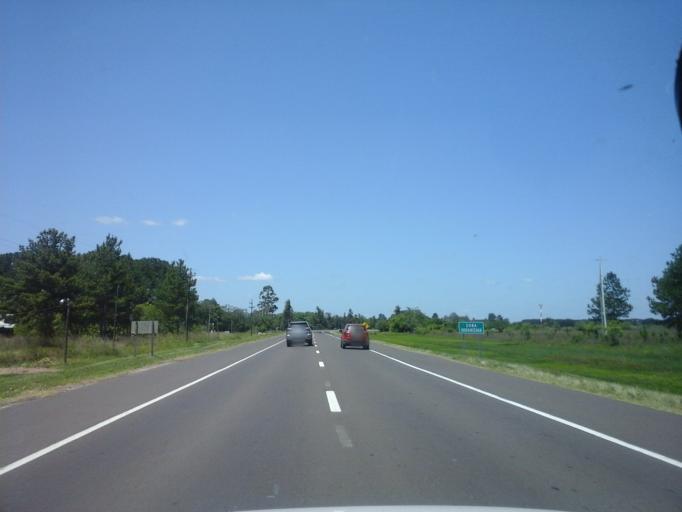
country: AR
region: Corrientes
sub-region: Departamento de San Cosme
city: San Cosme
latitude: -27.3782
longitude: -58.5229
